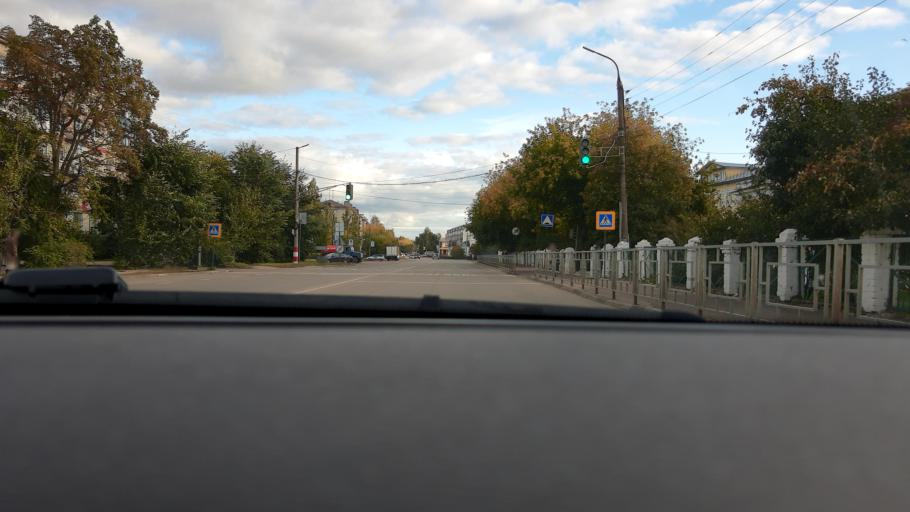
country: RU
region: Nizjnij Novgorod
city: Novaya Balakhna
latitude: 56.4997
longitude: 43.6046
